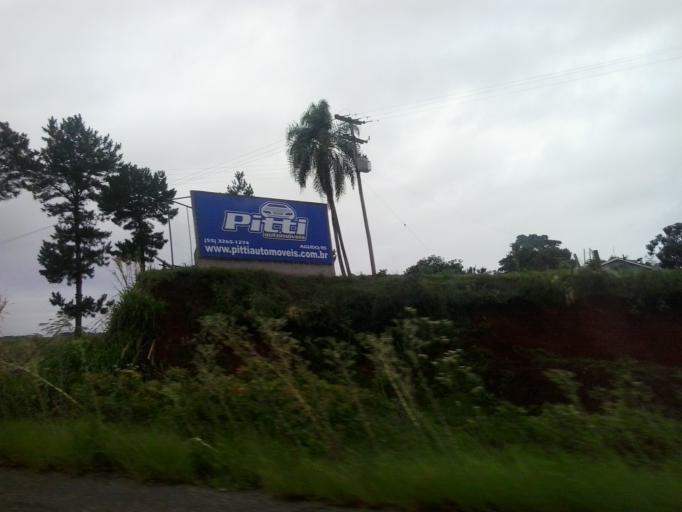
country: BR
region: Rio Grande do Sul
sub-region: Santa Maria
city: Santa Maria
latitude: -29.7227
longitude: -53.3687
